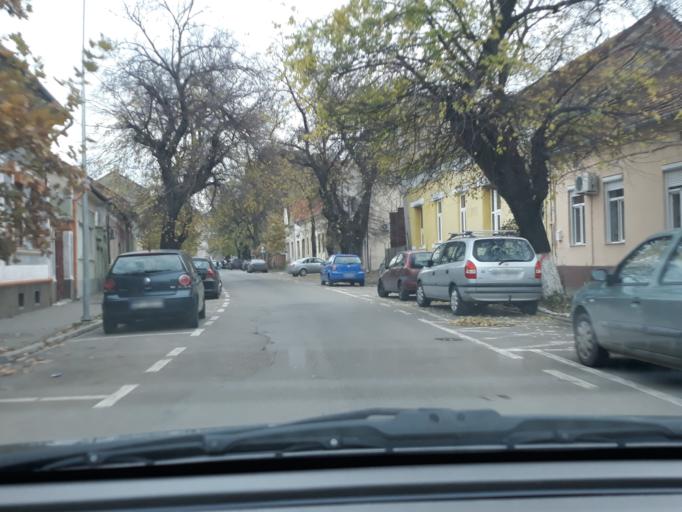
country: RO
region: Bihor
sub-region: Comuna Biharea
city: Oradea
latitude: 47.0633
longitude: 21.9291
